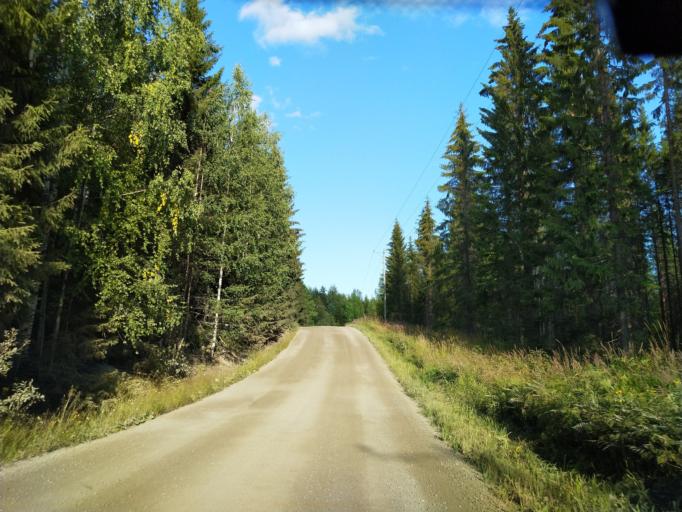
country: FI
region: Central Finland
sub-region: Jaemsae
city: Kuhmoinen
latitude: 61.6941
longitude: 24.9431
